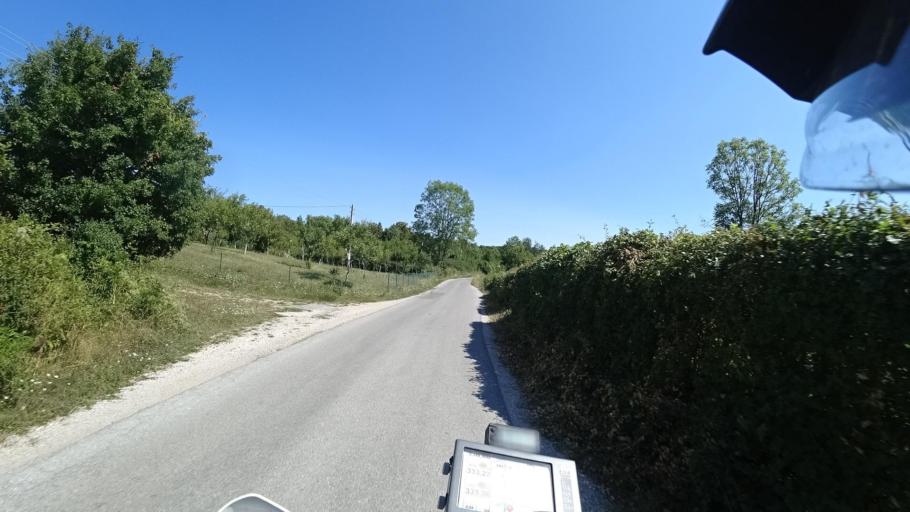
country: HR
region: Licko-Senjska
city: Popovaca
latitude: 44.7296
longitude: 15.2823
